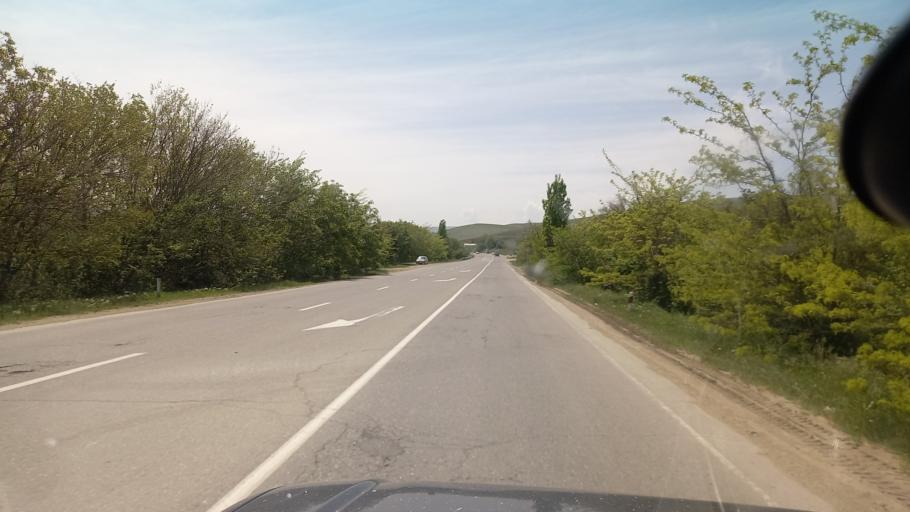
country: RU
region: Dagestan
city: Manas
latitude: 42.7108
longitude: 47.6436
